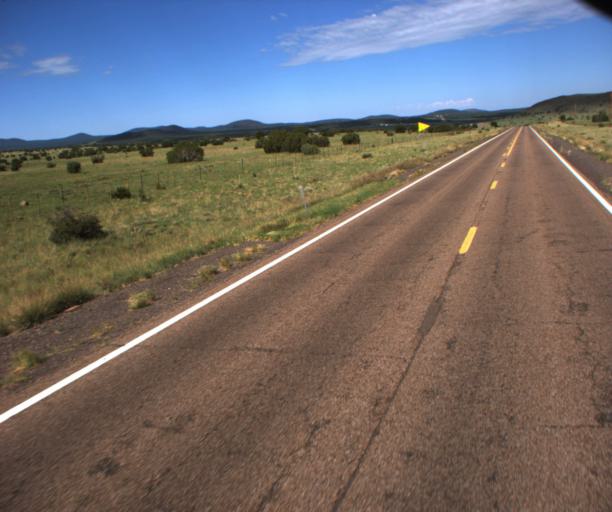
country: US
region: Arizona
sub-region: Apache County
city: Saint Johns
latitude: 34.2686
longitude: -109.6261
